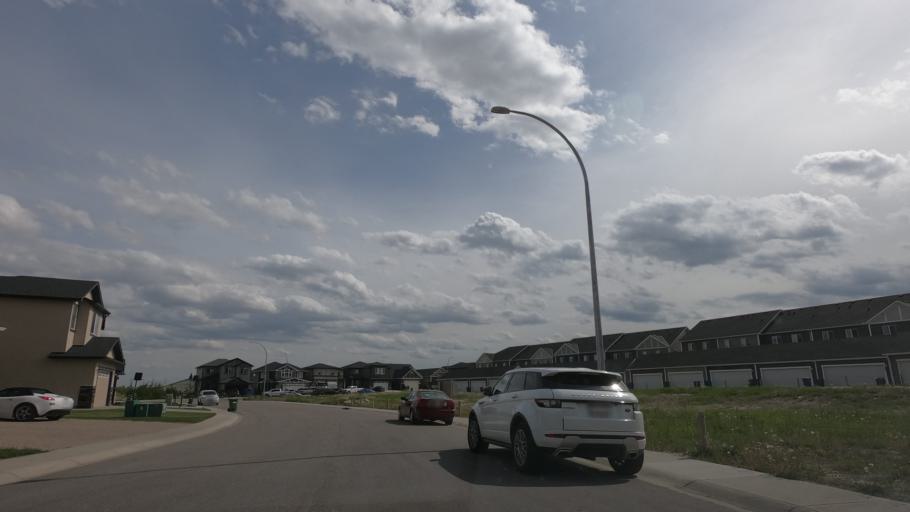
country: CA
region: Alberta
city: Airdrie
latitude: 51.2745
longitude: -114.0448
